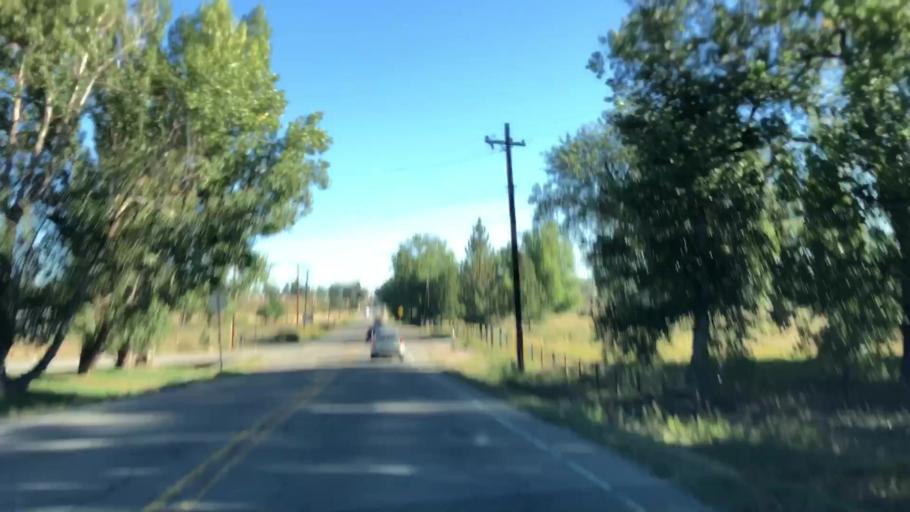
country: US
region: Colorado
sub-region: Larimer County
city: Loveland
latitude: 40.4008
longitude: -105.1230
